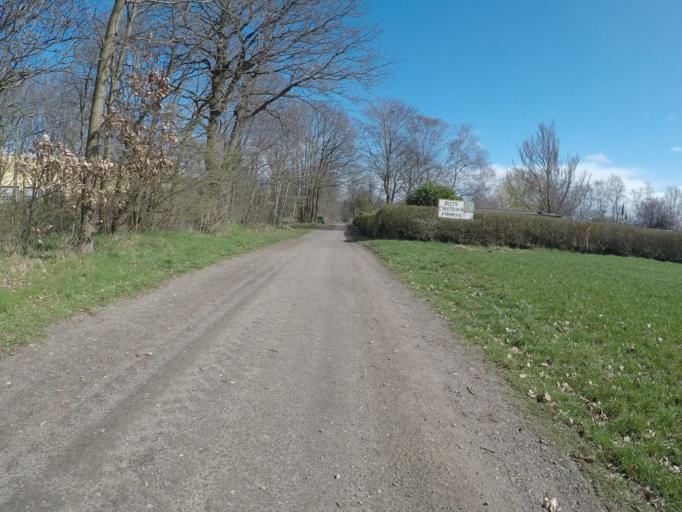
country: DE
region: Lower Saxony
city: Langen
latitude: 53.6084
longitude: 8.6128
